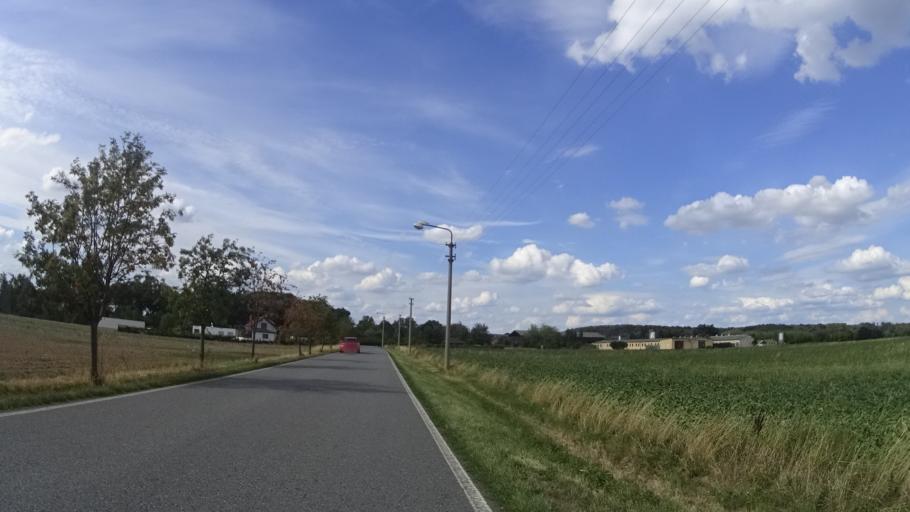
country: CZ
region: Olomoucky
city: Moravicany
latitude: 49.7419
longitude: 16.9738
